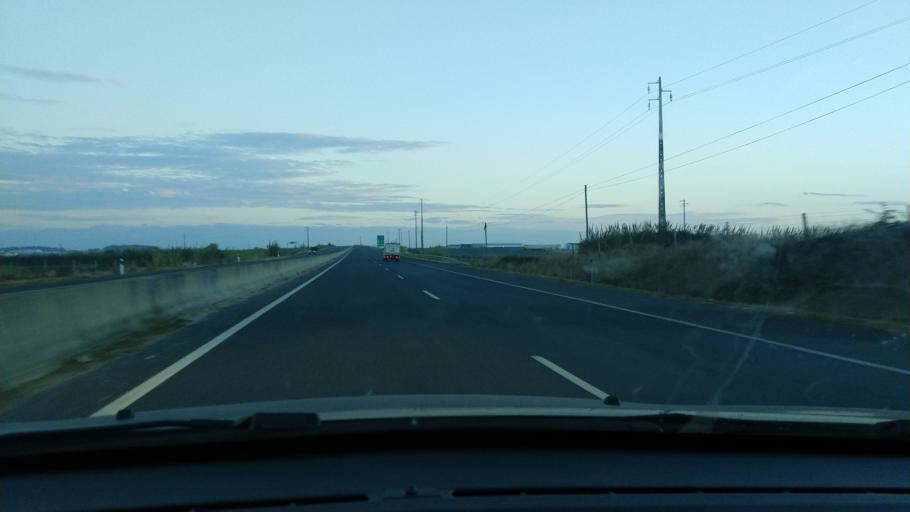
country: PT
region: Leiria
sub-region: Peniche
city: Atouguia da Baleia
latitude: 39.3387
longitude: -9.3376
